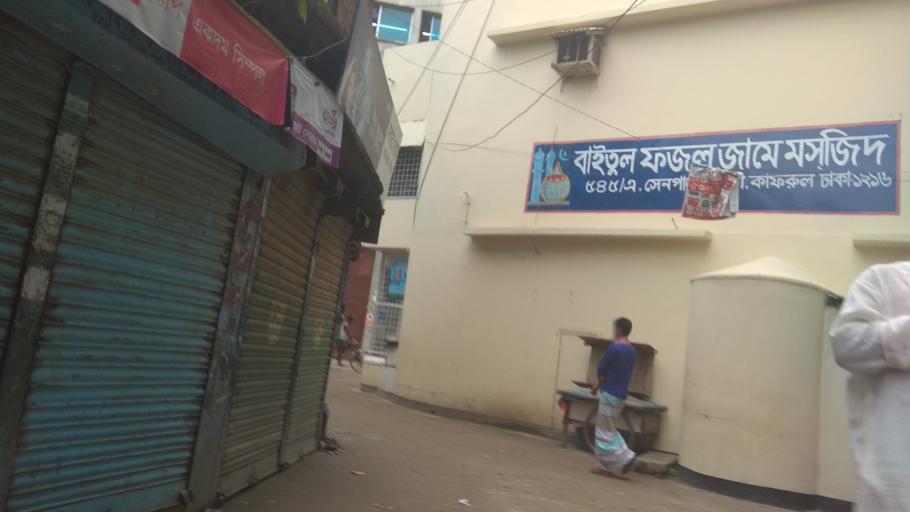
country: BD
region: Dhaka
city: Azimpur
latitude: 23.8019
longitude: 90.3778
